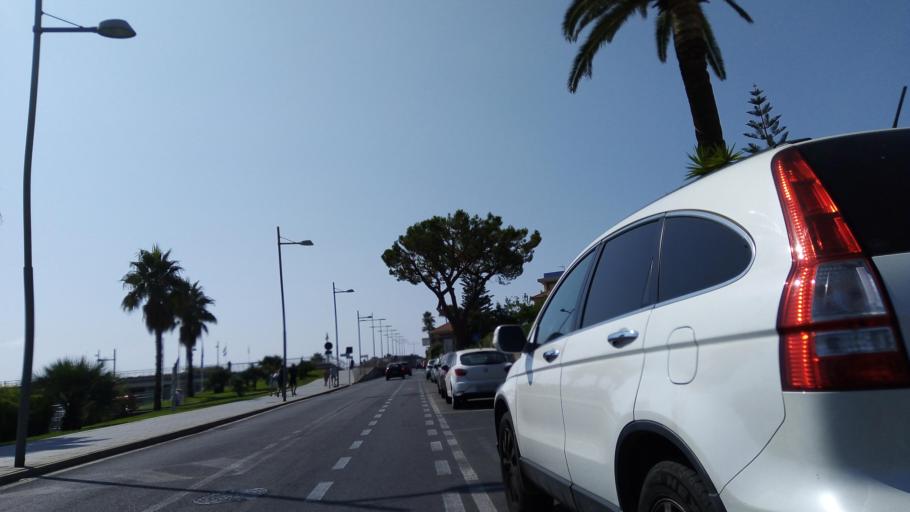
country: IT
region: Liguria
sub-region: Provincia di Savona
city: Loano
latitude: 44.1314
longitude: 8.2627
